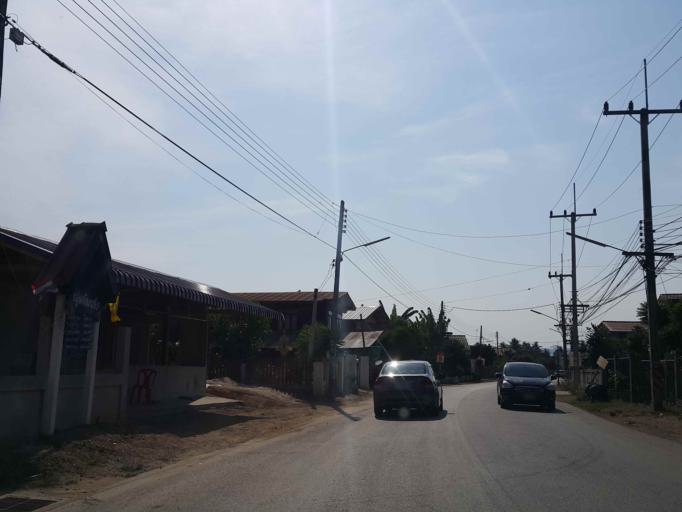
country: TH
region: Sukhothai
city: Thung Saliam
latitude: 17.3339
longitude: 99.5873
